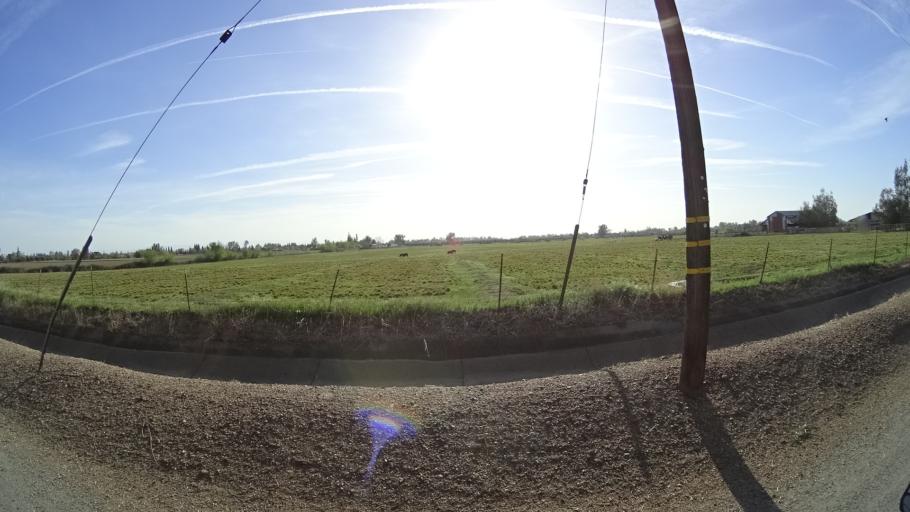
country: US
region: California
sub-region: Glenn County
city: Orland
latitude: 39.7323
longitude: -122.2347
